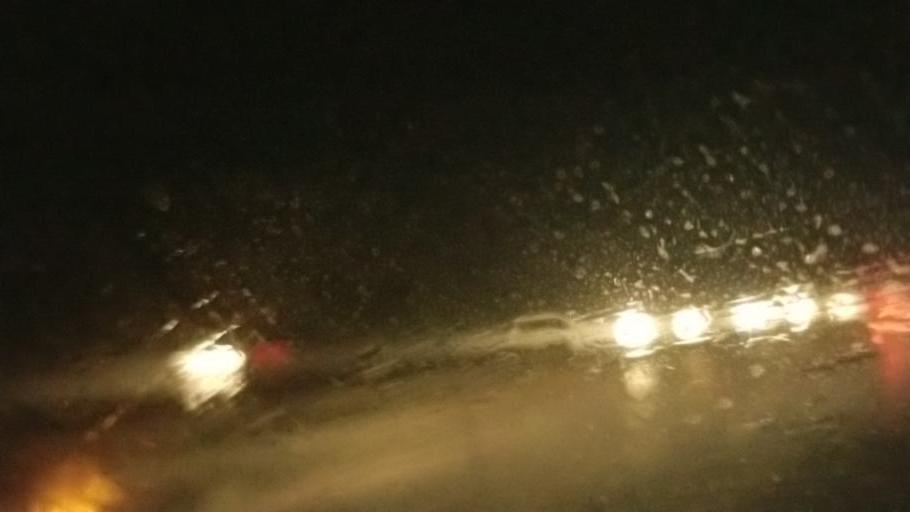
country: US
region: New York
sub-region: Cayuga County
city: Port Byron
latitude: 43.0345
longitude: -76.6427
